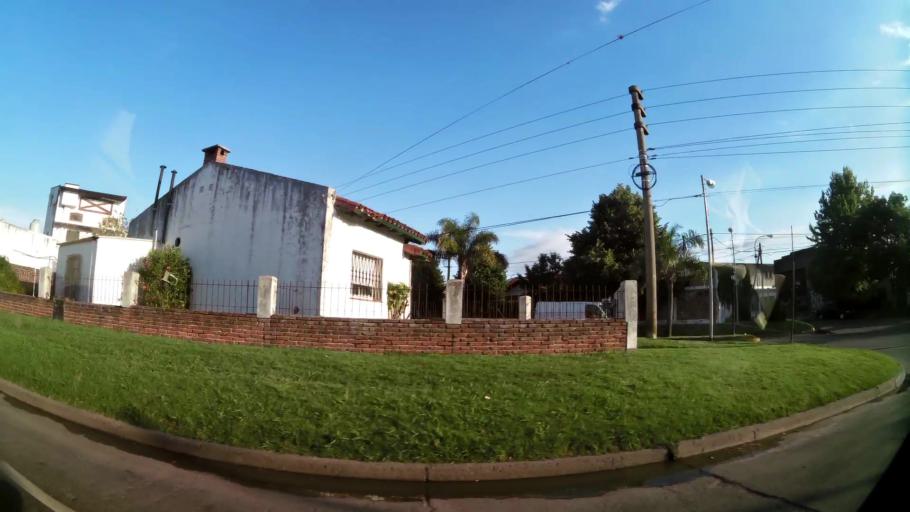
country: AR
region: Buenos Aires
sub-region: Partido de Tigre
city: Tigre
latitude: -34.4538
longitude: -58.6394
